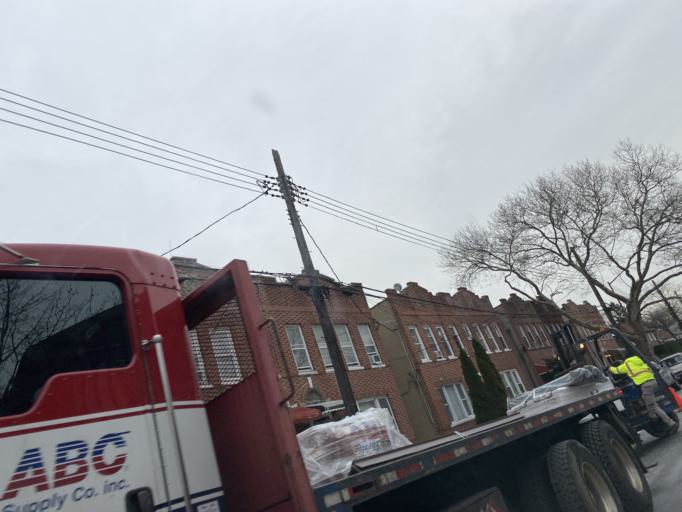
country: US
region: New York
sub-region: Kings County
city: Brooklyn
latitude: 40.6579
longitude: -73.9381
